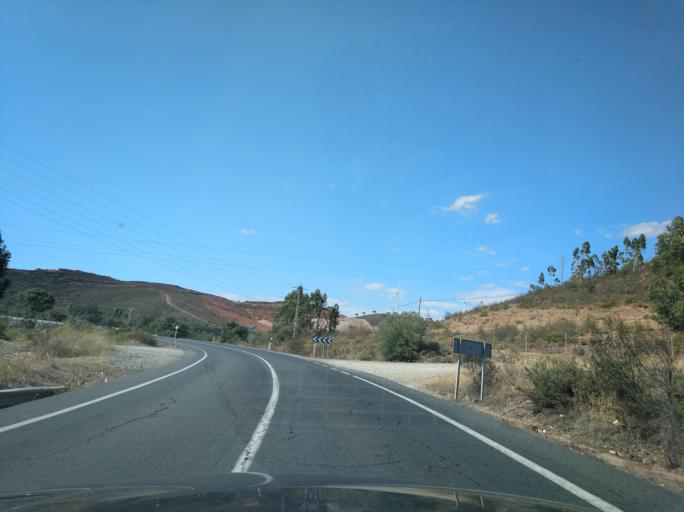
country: ES
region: Andalusia
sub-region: Provincia de Huelva
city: Alosno
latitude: 37.5782
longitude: -7.1128
